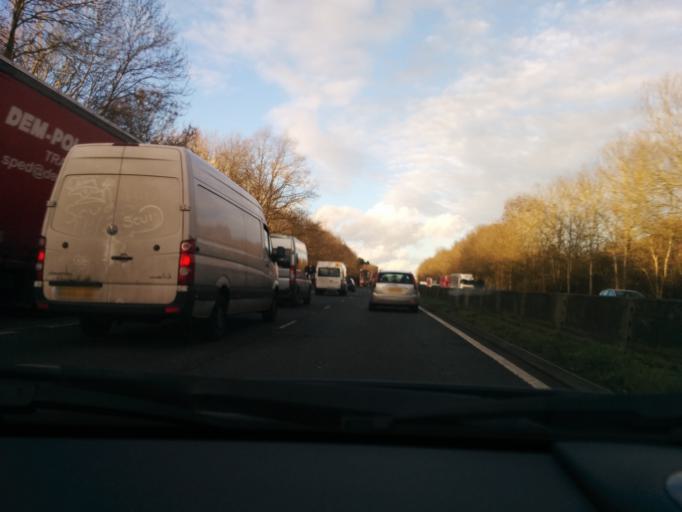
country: GB
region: England
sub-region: Oxfordshire
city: Cowley
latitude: 51.7492
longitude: -1.1955
